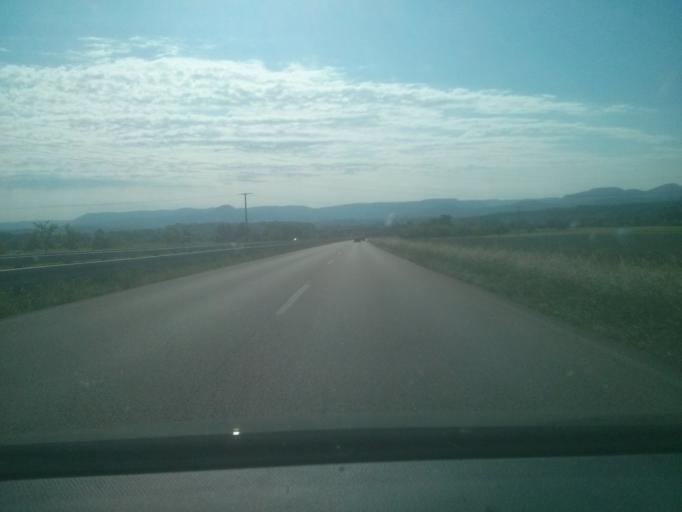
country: DE
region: Baden-Wuerttemberg
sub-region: Tuebingen Region
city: Kusterdingen
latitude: 48.5054
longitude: 9.1136
